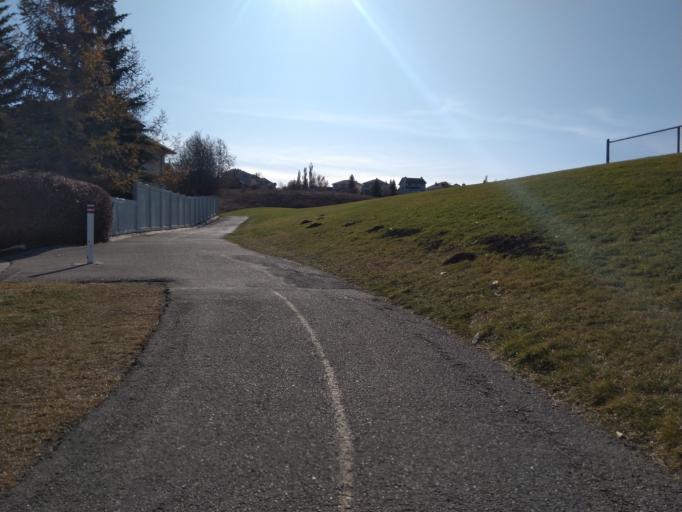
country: CA
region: Alberta
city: Calgary
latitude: 51.1502
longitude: -114.1097
